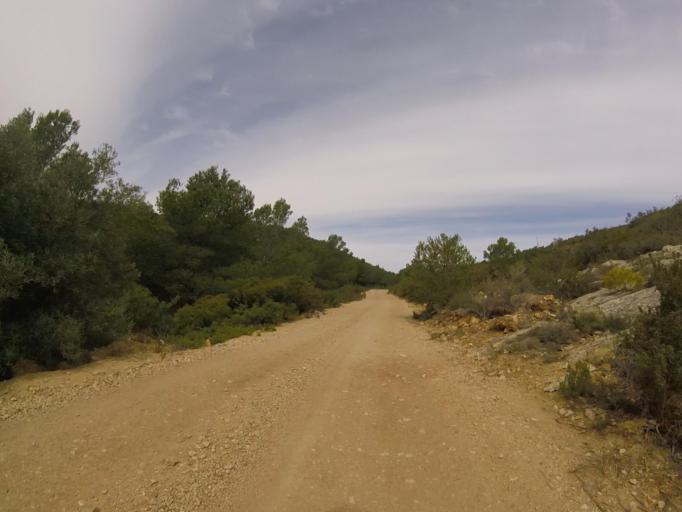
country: ES
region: Valencia
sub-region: Provincia de Castello
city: Cabanes
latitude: 40.1906
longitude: 0.0867
